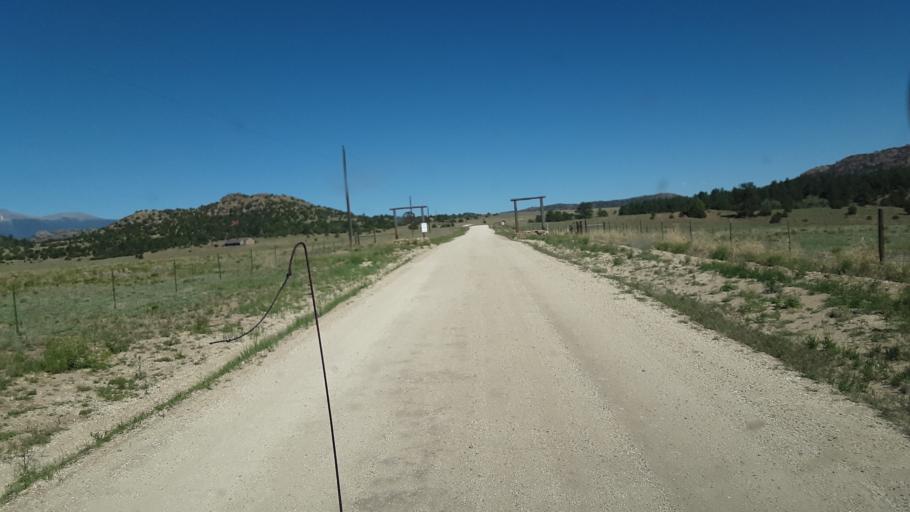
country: US
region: Colorado
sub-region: Custer County
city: Westcliffe
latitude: 38.2165
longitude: -105.4492
